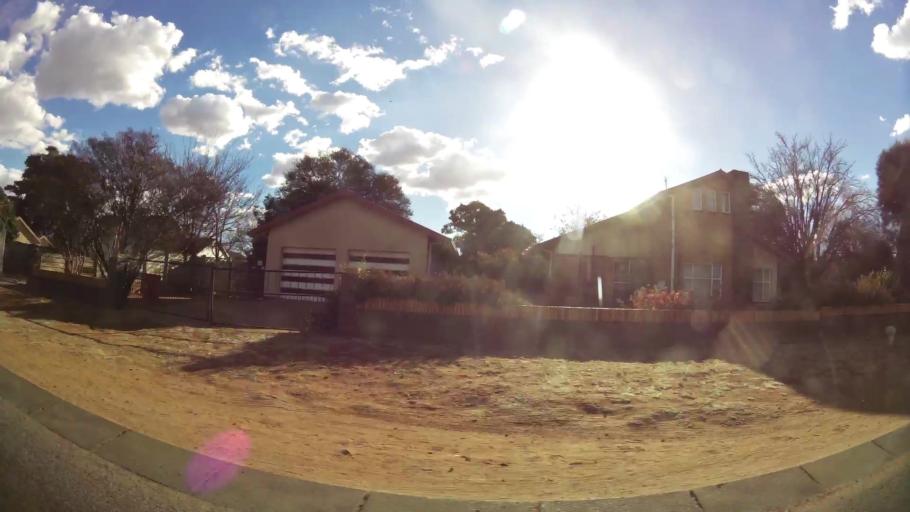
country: ZA
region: North-West
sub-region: Dr Kenneth Kaunda District Municipality
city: Klerksdorp
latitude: -26.8414
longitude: 26.6571
